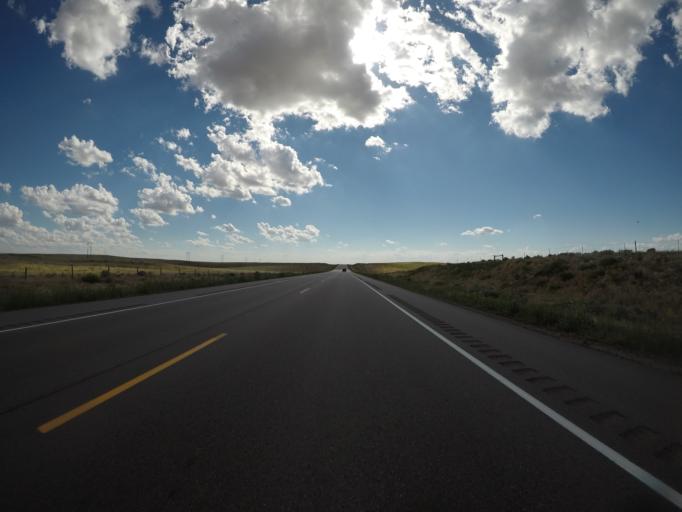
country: US
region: Colorado
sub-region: Logan County
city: Sterling
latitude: 40.6320
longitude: -103.1274
